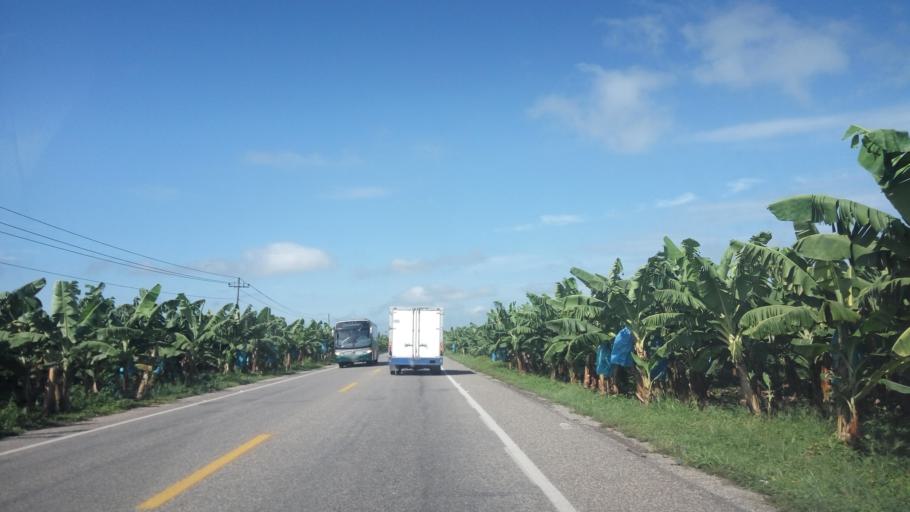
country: MX
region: Tabasco
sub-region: Teapa
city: Eureka y Belen
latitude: 17.6543
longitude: -92.9563
